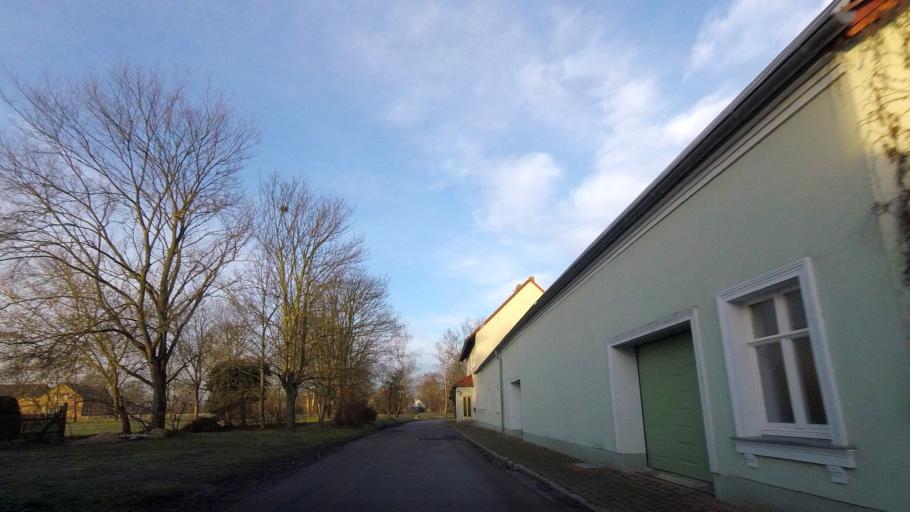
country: DE
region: Brandenburg
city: Niedergorsdorf
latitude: 51.9744
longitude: 12.9240
